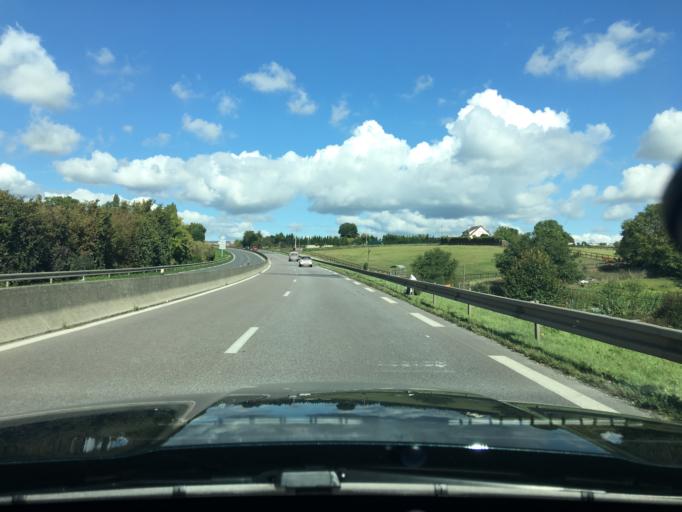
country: FR
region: Ile-de-France
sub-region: Departement du Val-d'Oise
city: Louvres
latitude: 49.0389
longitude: 2.5089
